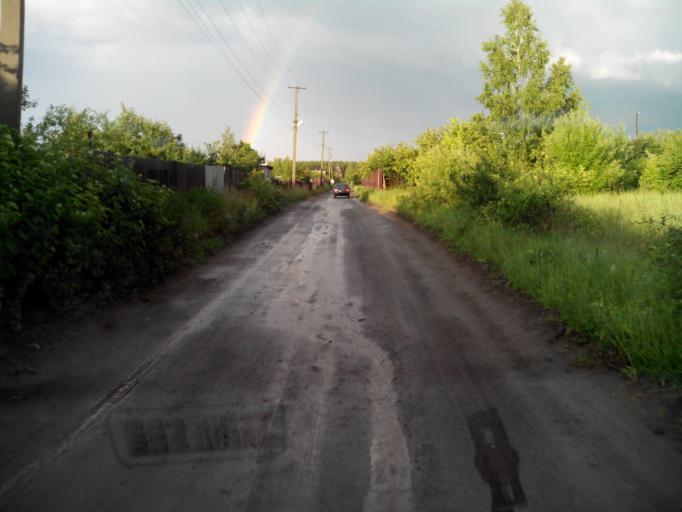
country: RU
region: Penza
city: Zasechnoye
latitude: 53.0387
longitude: 45.0451
